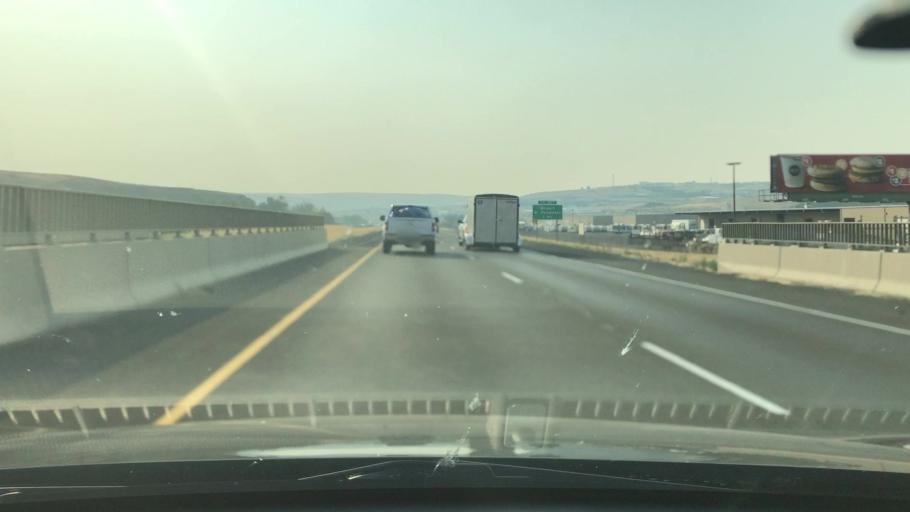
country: US
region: Oregon
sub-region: Umatilla County
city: Pendleton
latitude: 45.6666
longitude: -118.8179
